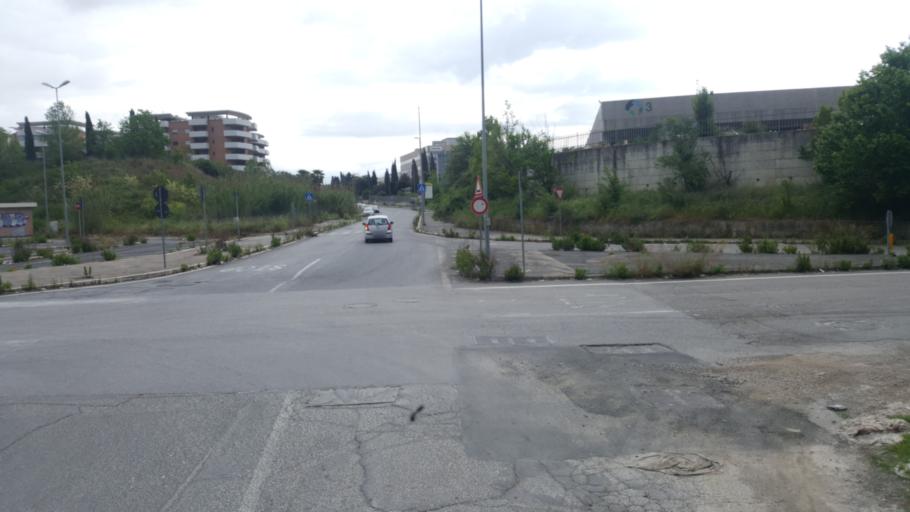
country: IT
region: Latium
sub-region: Citta metropolitana di Roma Capitale
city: Setteville
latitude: 41.9327
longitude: 12.6155
